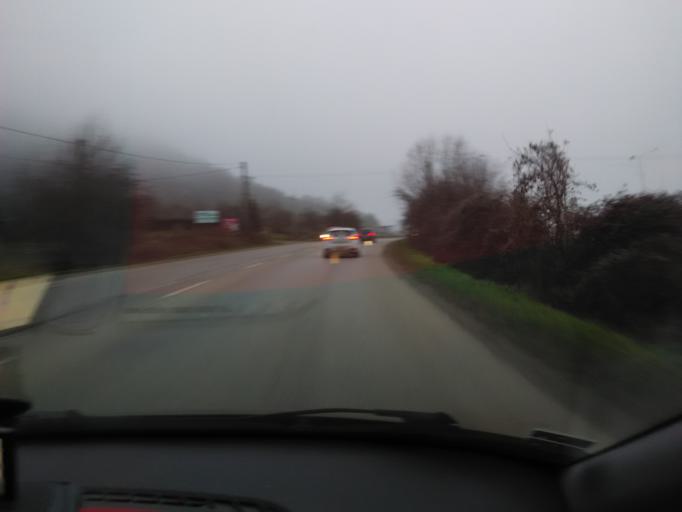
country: SK
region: Trenciansky
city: Nova Dubnica
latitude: 48.9304
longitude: 18.1161
